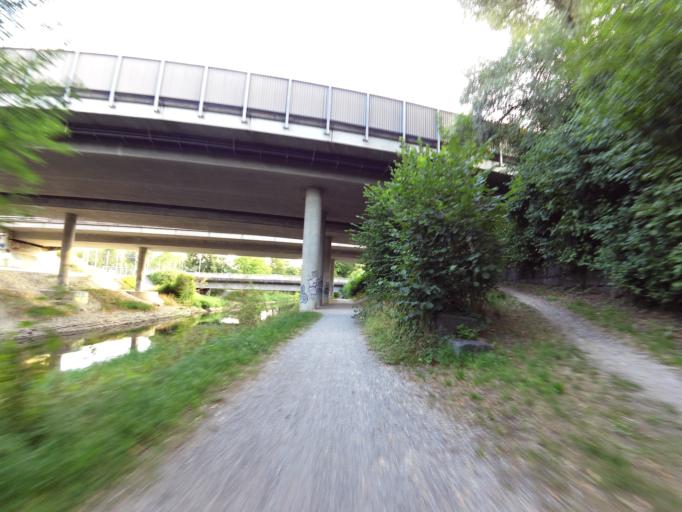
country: CH
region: Zurich
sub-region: Bezirk Buelach
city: Grossacker/Opfikon
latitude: 47.4242
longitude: 8.5723
